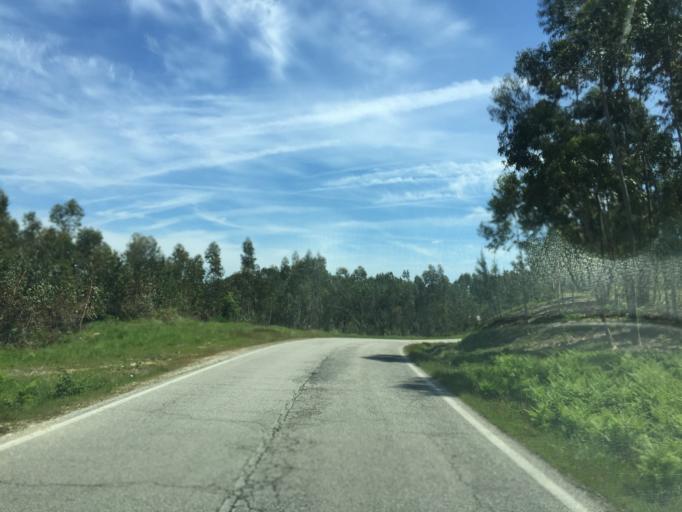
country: PT
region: Coimbra
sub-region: Soure
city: Soure
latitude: 40.0553
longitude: -8.6808
